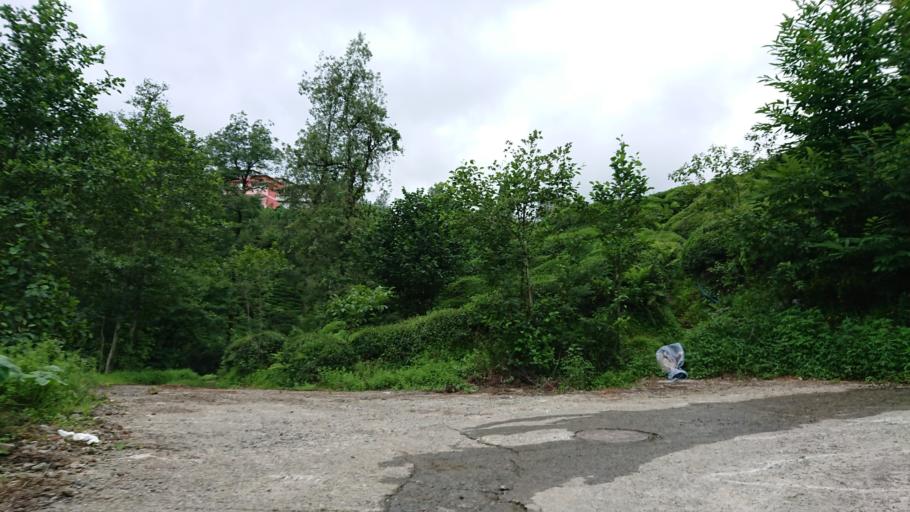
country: TR
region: Rize
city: Rize
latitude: 40.9666
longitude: 40.5158
